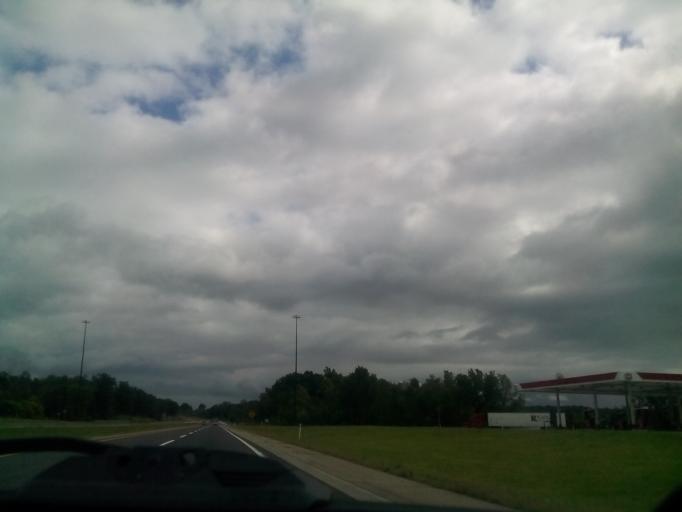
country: US
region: Indiana
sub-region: Steuben County
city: Fremont
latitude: 41.7260
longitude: -84.9671
